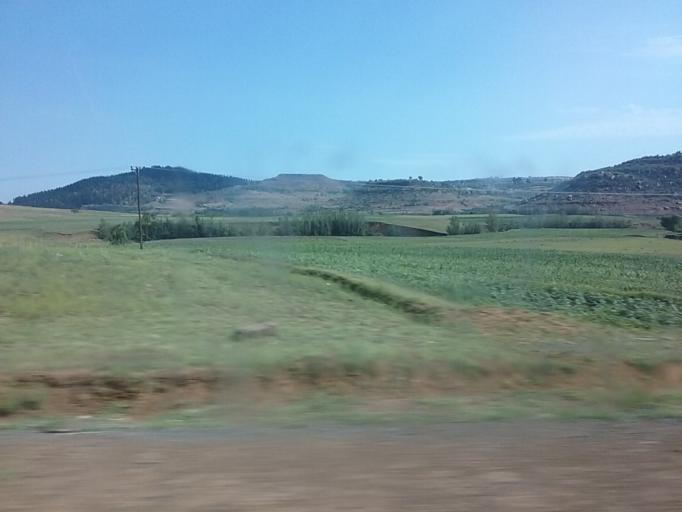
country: LS
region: Leribe
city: Maputsoe
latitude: -29.0876
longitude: 27.9473
